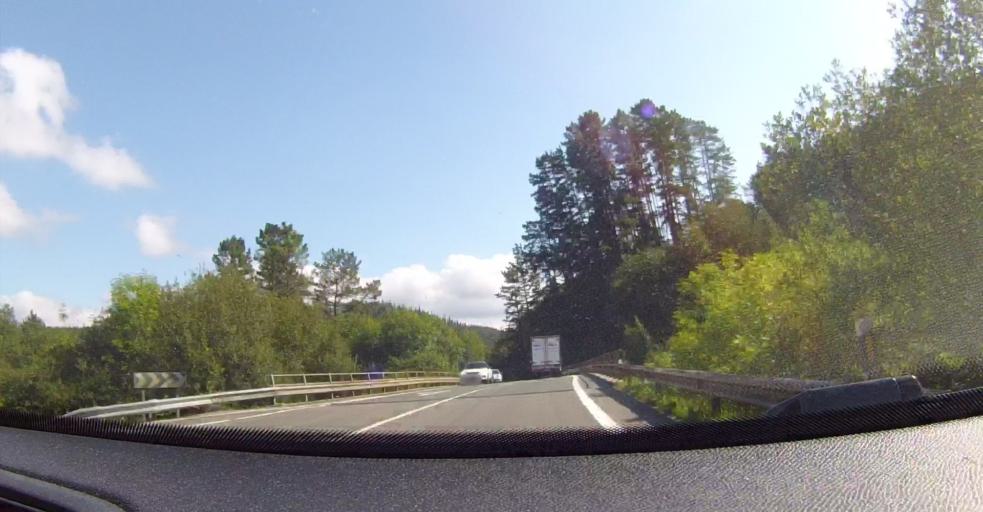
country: ES
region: Basque Country
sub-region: Bizkaia
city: Muxika
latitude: 43.2556
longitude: -2.6910
